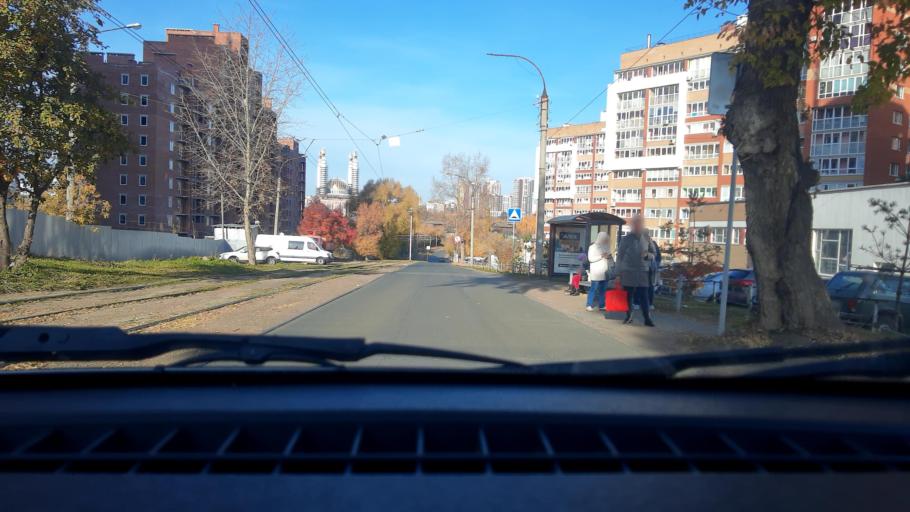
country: RU
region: Bashkortostan
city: Ufa
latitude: 54.7142
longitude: 55.9774
